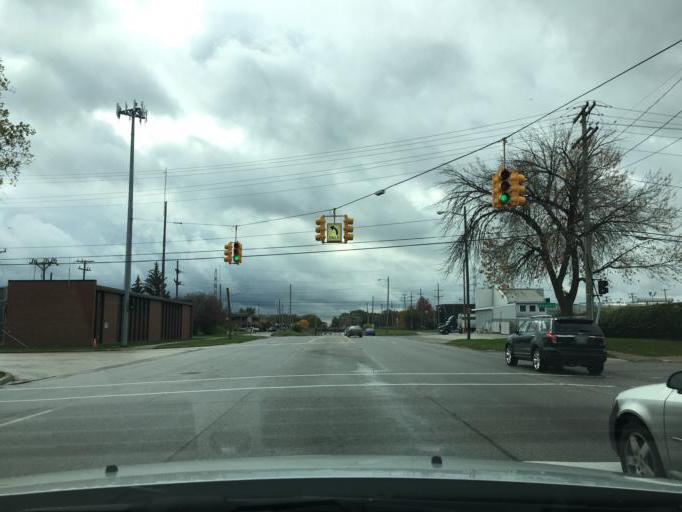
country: US
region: Michigan
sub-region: Wayne County
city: Redford
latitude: 42.3809
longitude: -83.2953
